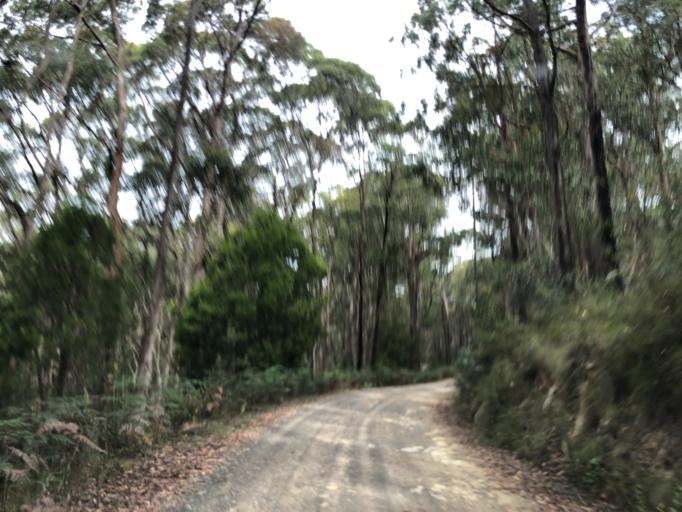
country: AU
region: Victoria
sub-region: Moorabool
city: Bacchus Marsh
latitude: -37.4640
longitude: 144.2775
